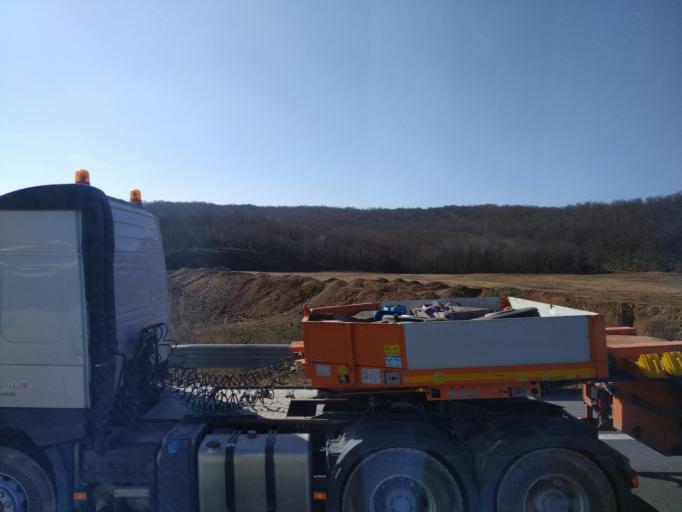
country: TR
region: Istanbul
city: Mahmut Sevket Pasa
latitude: 41.1639
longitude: 29.2564
